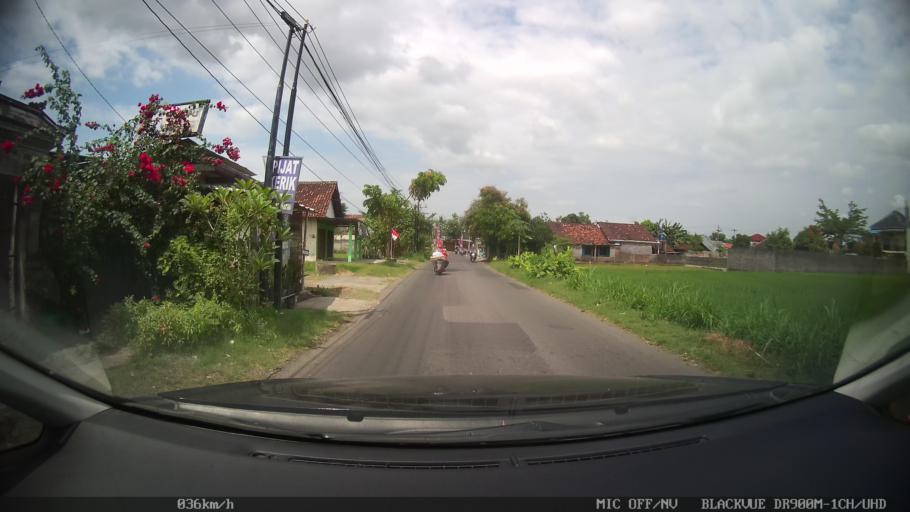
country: ID
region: Daerah Istimewa Yogyakarta
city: Depok
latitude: -7.7939
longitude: 110.4582
